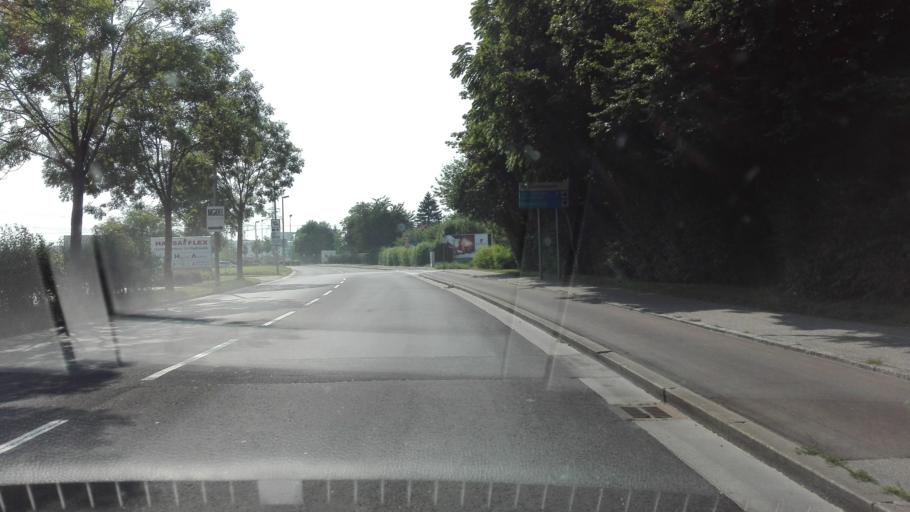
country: AT
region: Upper Austria
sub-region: Politischer Bezirk Linz-Land
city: Ansfelden
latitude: 48.2425
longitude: 14.2895
